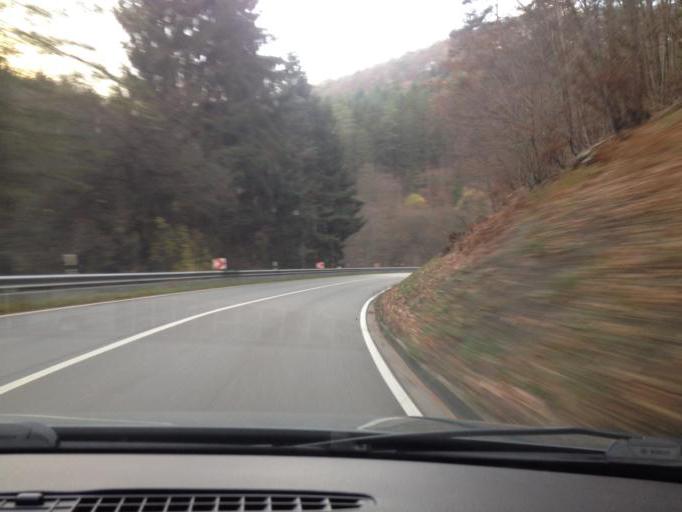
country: DE
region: Rheinland-Pfalz
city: Weidenthal
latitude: 49.4090
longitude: 8.0079
